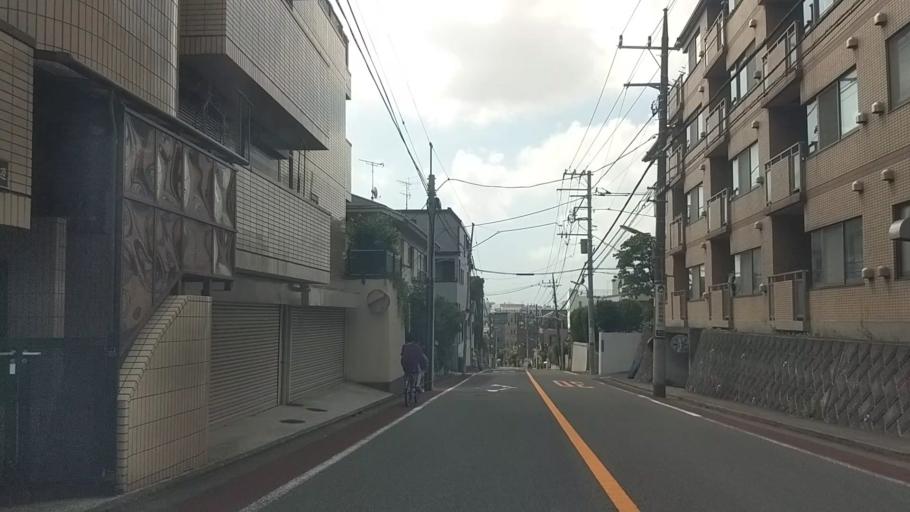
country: JP
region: Kanagawa
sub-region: Kawasaki-shi
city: Kawasaki
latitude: 35.5849
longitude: 139.7161
